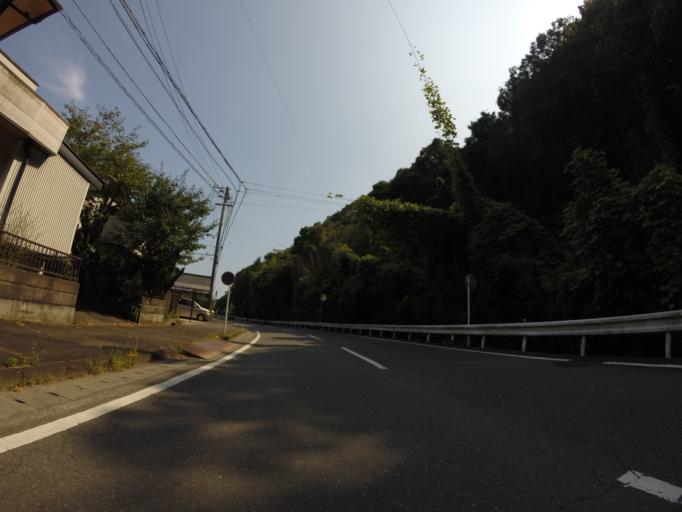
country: JP
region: Shizuoka
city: Shizuoka-shi
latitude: 35.0497
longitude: 138.3656
